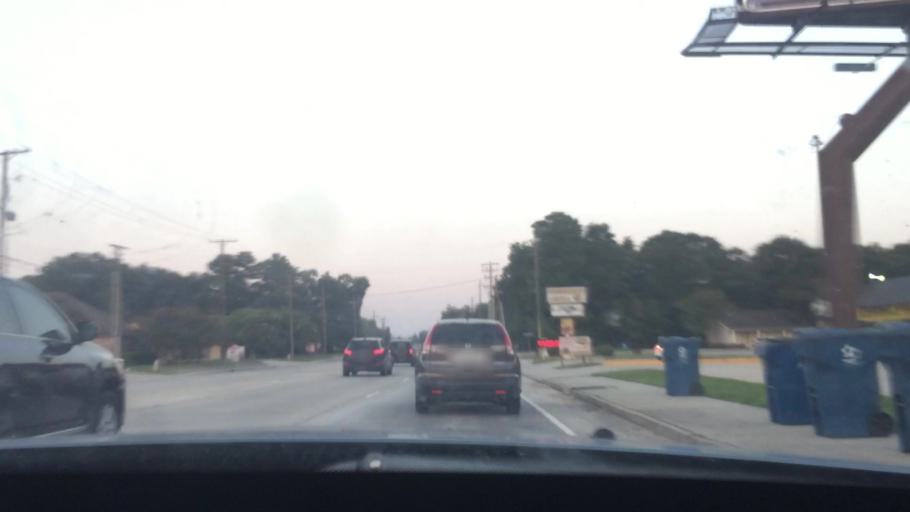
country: US
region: Louisiana
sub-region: East Baton Rouge Parish
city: Shenandoah
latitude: 30.4298
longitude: -91.0243
